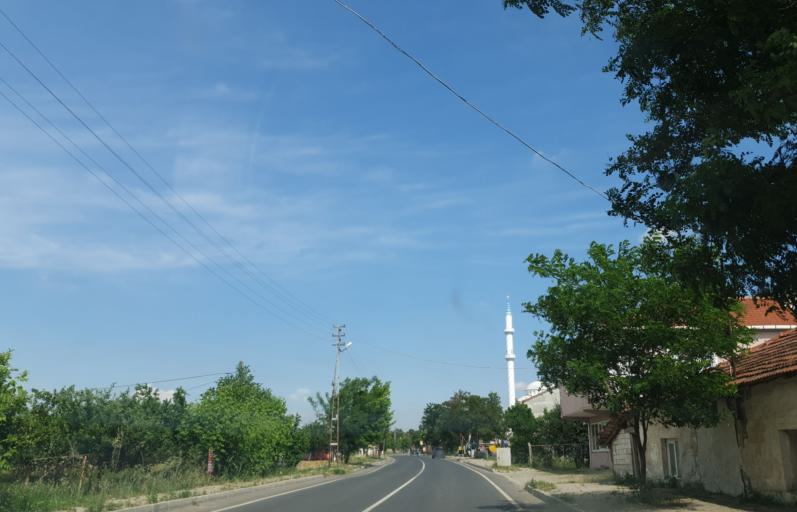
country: TR
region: Kirklareli
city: Buyukkaristiran
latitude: 41.2611
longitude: 27.6420
